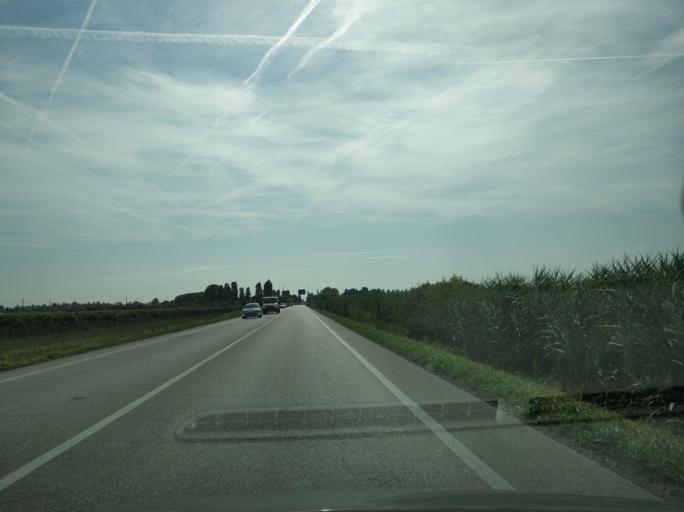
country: IT
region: Veneto
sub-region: Provincia di Padova
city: Bagnoli di Sopra
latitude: 45.2124
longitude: 11.8973
